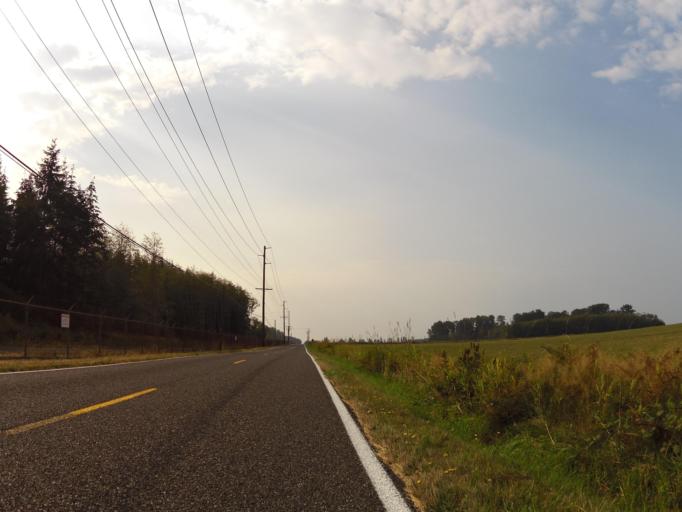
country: US
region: Washington
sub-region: Whatcom County
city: Birch Bay
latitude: 48.8807
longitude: -122.7490
